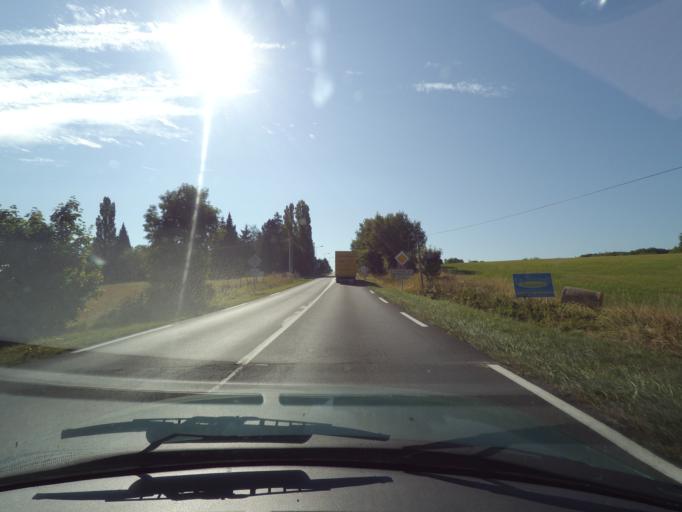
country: FR
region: Poitou-Charentes
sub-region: Departement de la Vienne
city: Terce
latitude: 46.4381
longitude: 0.5902
